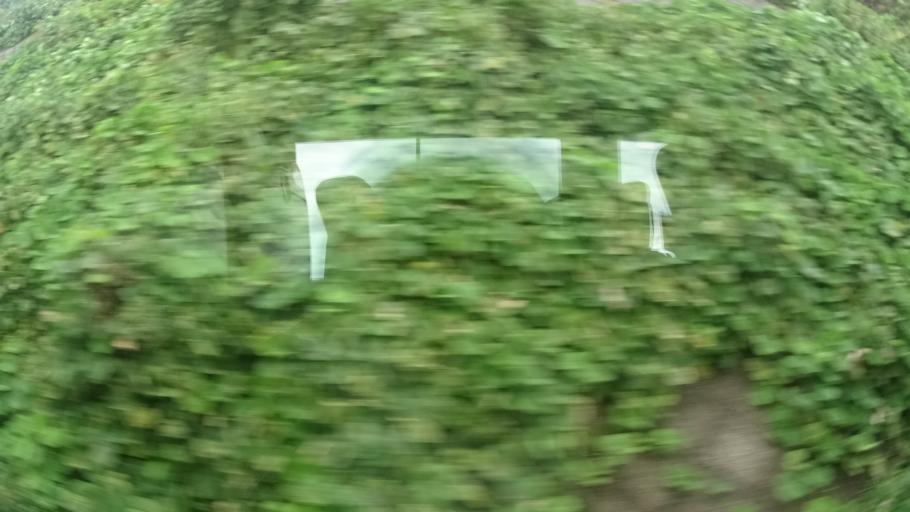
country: JP
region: Niigata
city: Murakami
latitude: 38.2454
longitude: 139.4439
